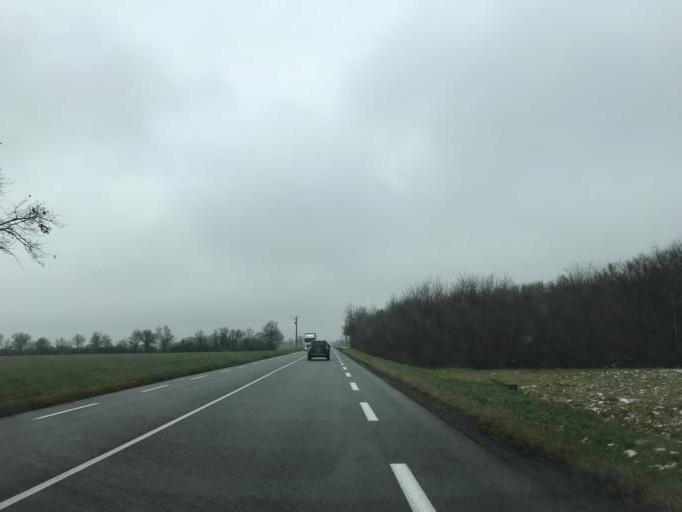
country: FR
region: Rhone-Alpes
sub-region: Departement de l'Ain
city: Villars-les-Dombes
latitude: 46.0310
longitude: 5.0624
